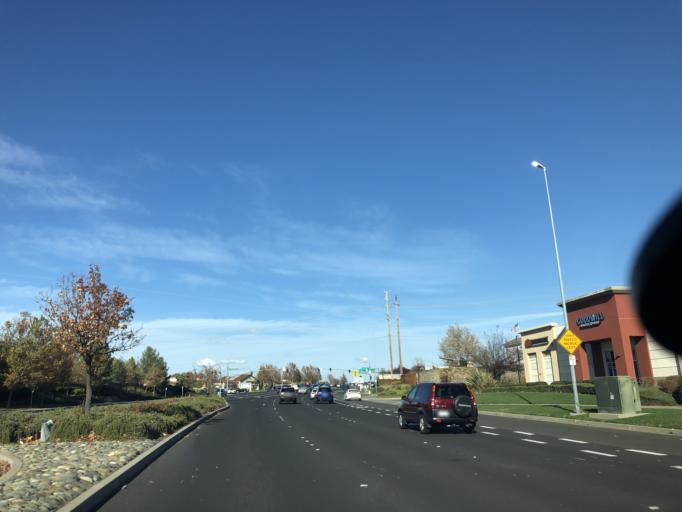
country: US
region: California
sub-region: Placer County
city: Roseville
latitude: 38.7815
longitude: -121.2868
